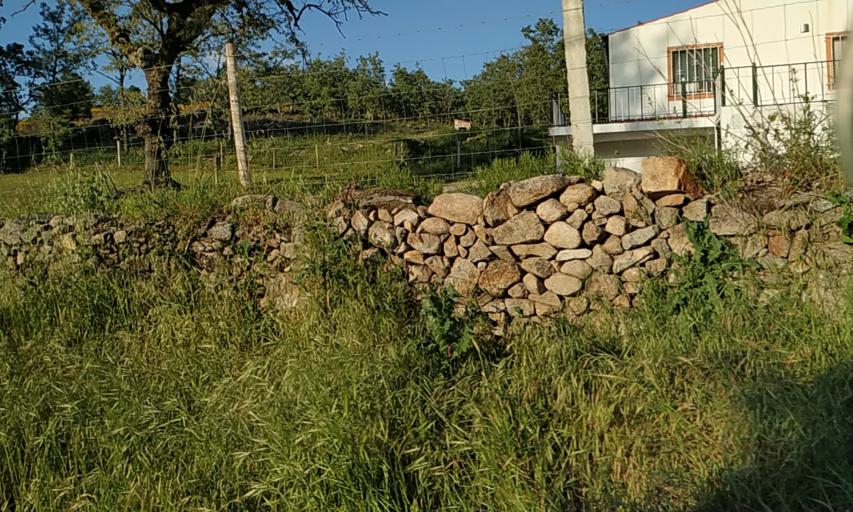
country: PT
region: Portalegre
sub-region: Marvao
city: Marvao
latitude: 39.3533
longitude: -7.4062
